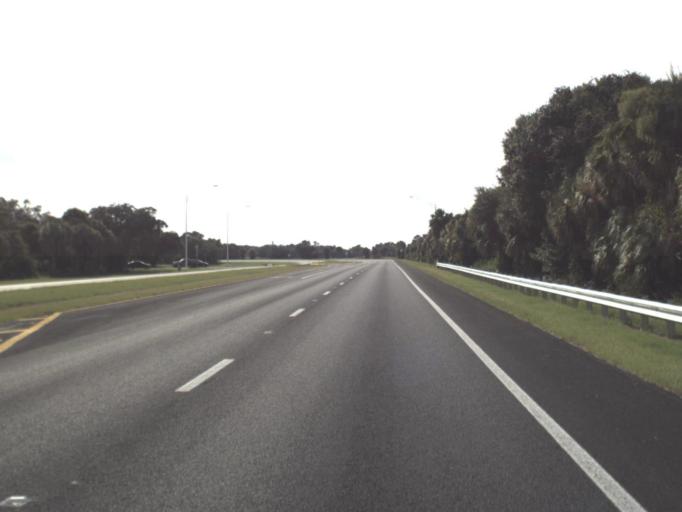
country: US
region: Florida
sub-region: Hendry County
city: Port LaBelle
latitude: 26.7686
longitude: -81.3728
